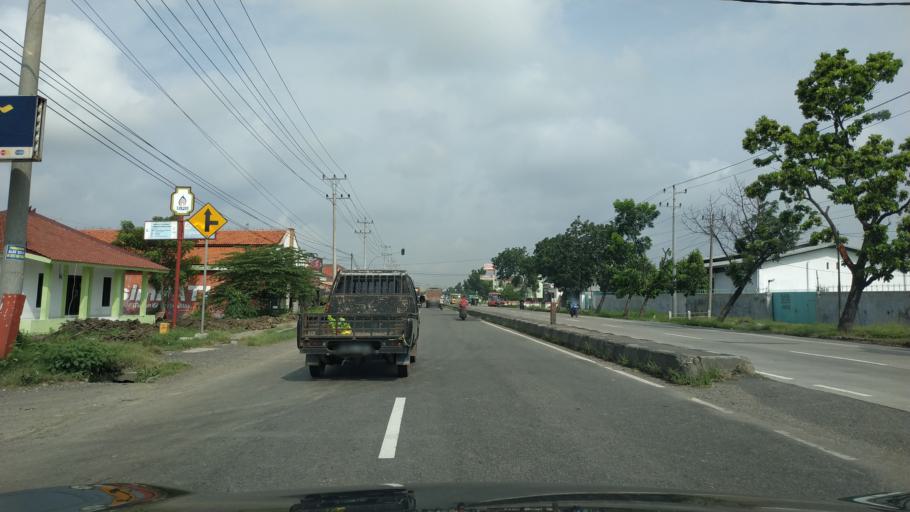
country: ID
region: Central Java
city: Bulakamba
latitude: -6.8747
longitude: 108.9332
